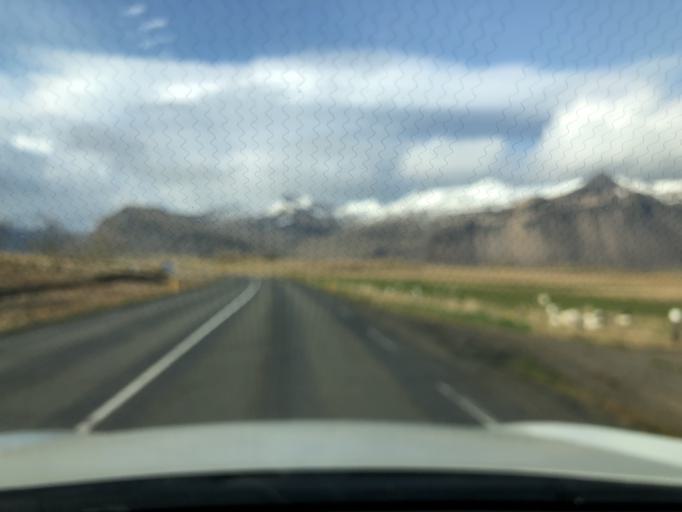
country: IS
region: East
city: Hoefn
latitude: 64.2856
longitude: -15.1856
